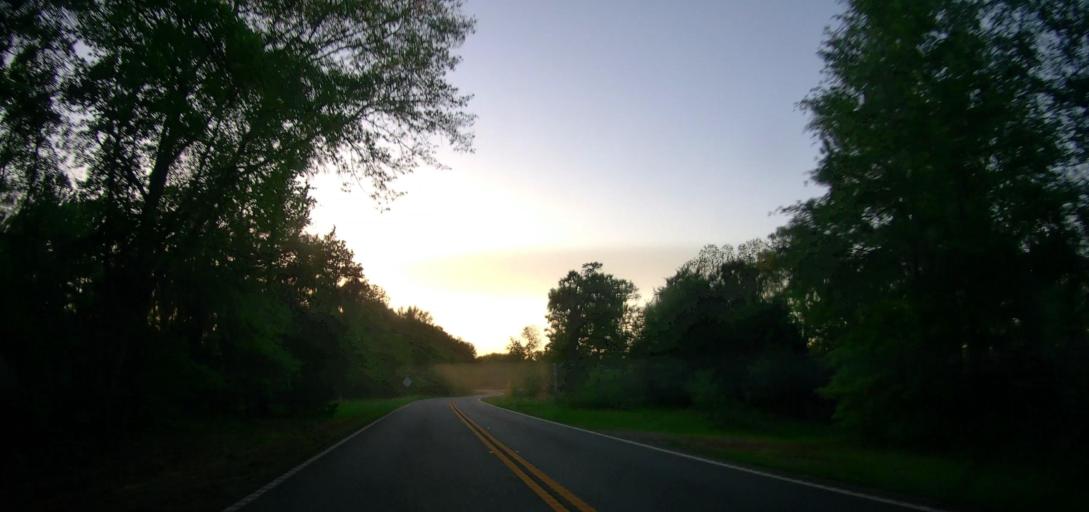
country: US
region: Georgia
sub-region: Marion County
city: Buena Vista
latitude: 32.3681
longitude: -84.5421
